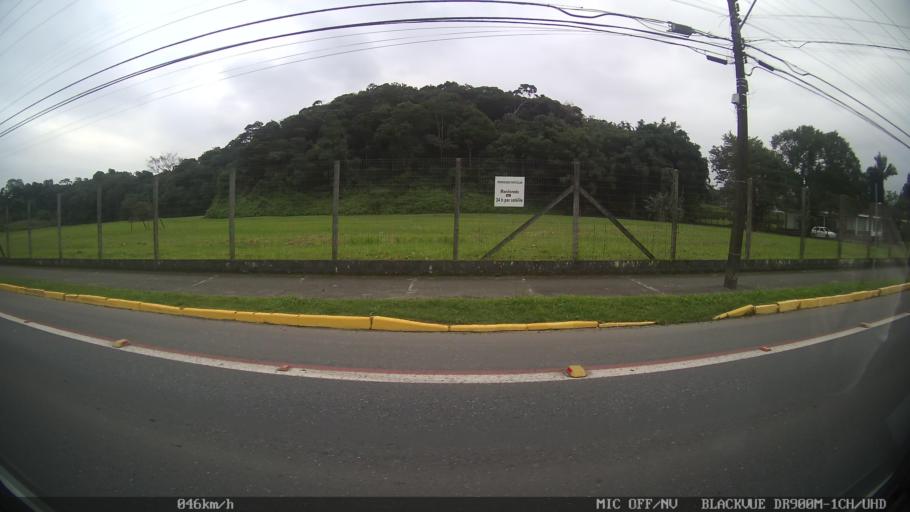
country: BR
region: Santa Catarina
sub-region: Joinville
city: Joinville
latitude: -26.2845
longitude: -48.8573
